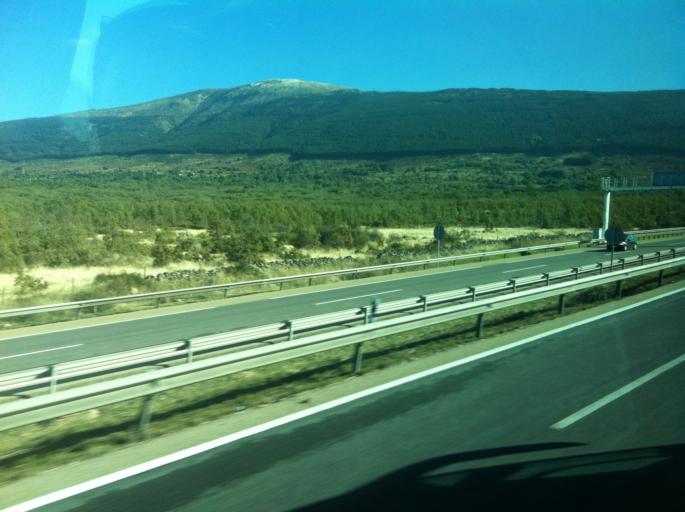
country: ES
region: Castille and Leon
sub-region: Provincia de Segovia
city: Cerezo de Abajo
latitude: 41.1825
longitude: -3.5846
